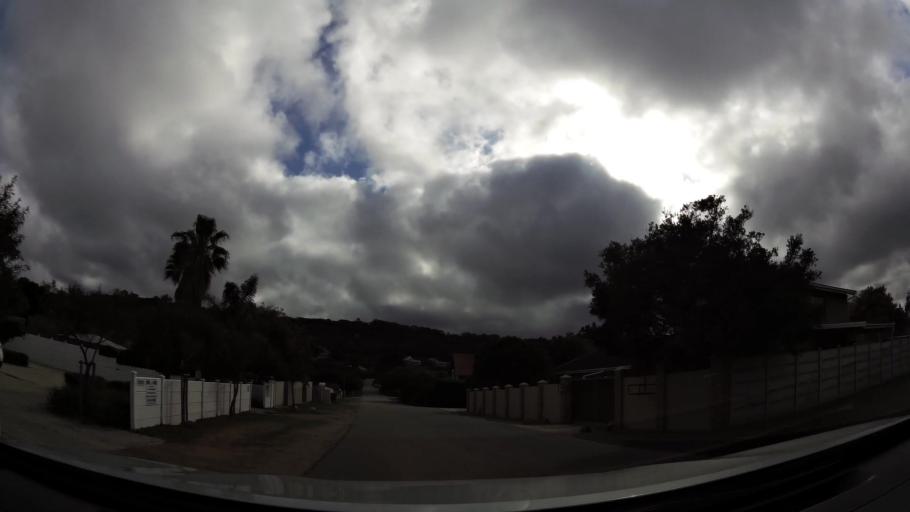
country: ZA
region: Western Cape
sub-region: Eden District Municipality
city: Plettenberg Bay
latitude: -34.0801
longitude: 23.3658
